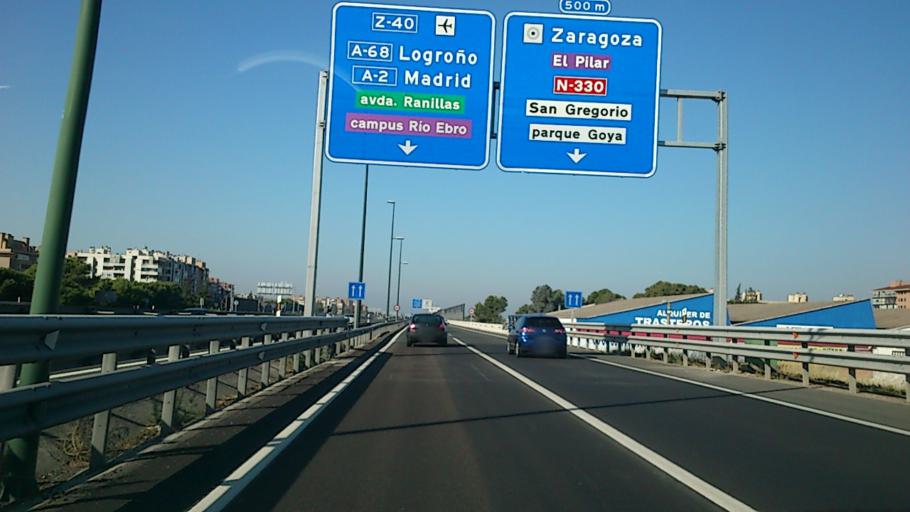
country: ES
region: Aragon
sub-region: Provincia de Zaragoza
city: Zaragoza
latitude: 41.6799
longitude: -0.8668
